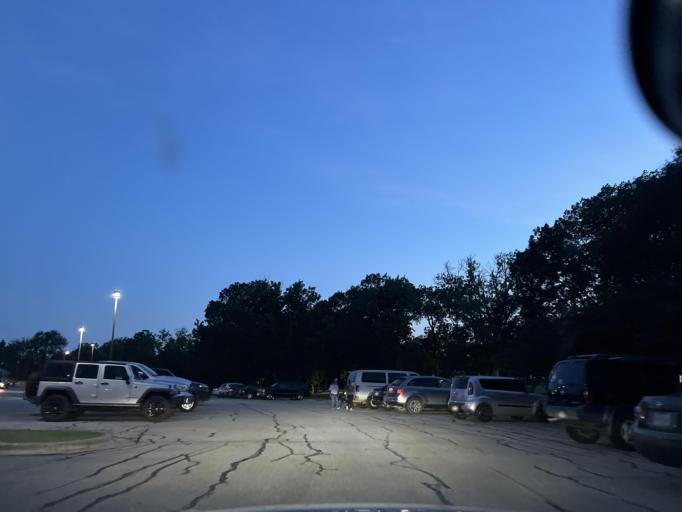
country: US
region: Texas
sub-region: Washington County
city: Brenham
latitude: 30.1856
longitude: -96.4049
